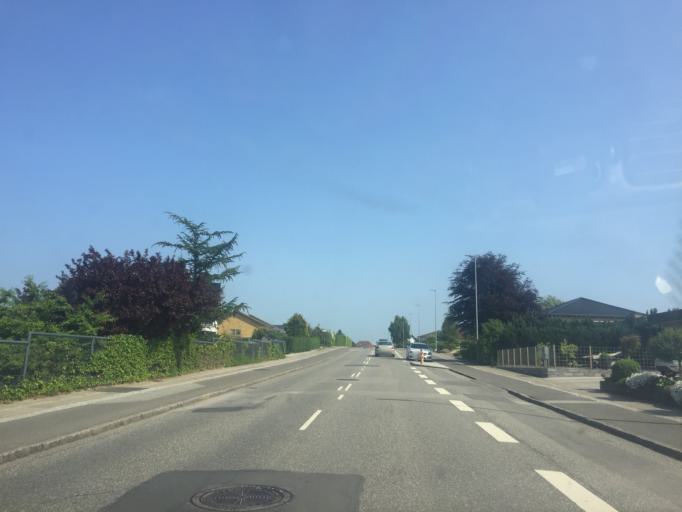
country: DK
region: South Denmark
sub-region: Kolding Kommune
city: Kolding
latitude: 55.4784
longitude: 9.4918
